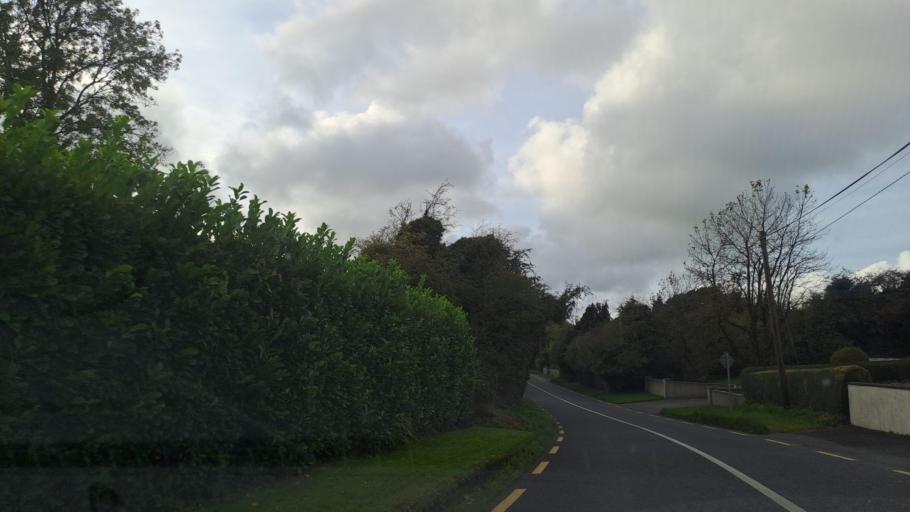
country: IE
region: Ulster
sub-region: An Cabhan
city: Kingscourt
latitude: 53.8681
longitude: -6.7990
